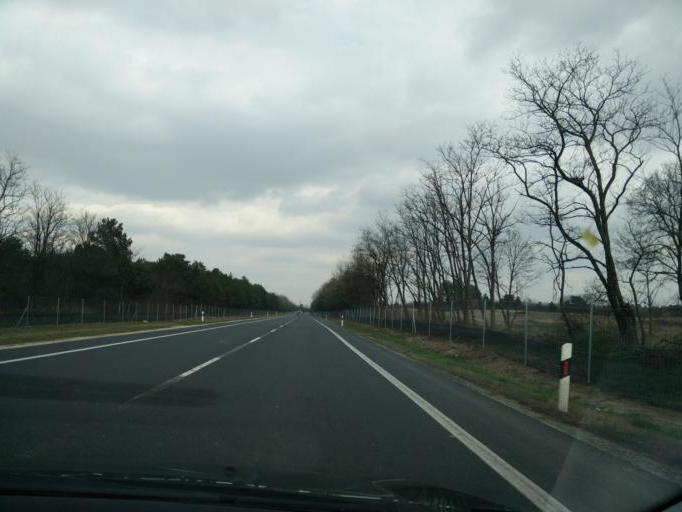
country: HU
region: Gyor-Moson-Sopron
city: Gyor
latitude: 47.7160
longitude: 17.6966
